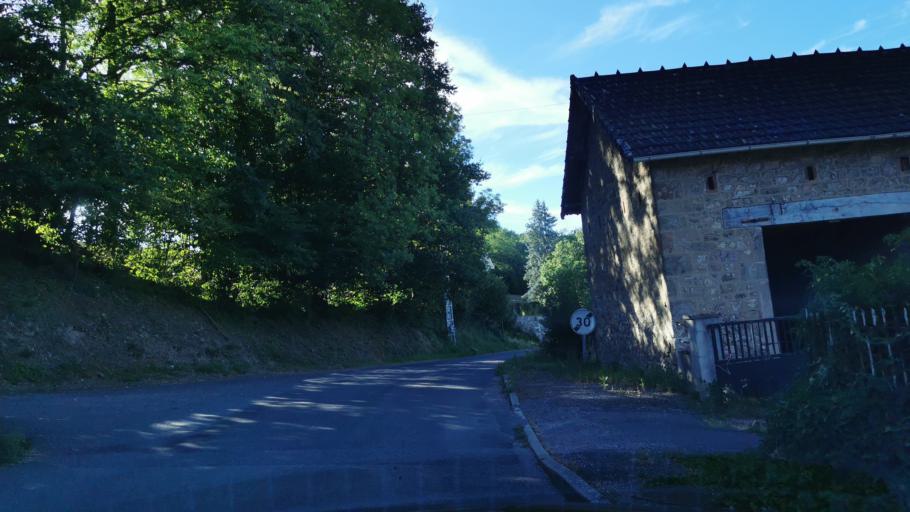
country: FR
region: Bourgogne
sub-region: Departement de Saone-et-Loire
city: Marmagne
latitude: 46.8412
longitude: 4.3279
